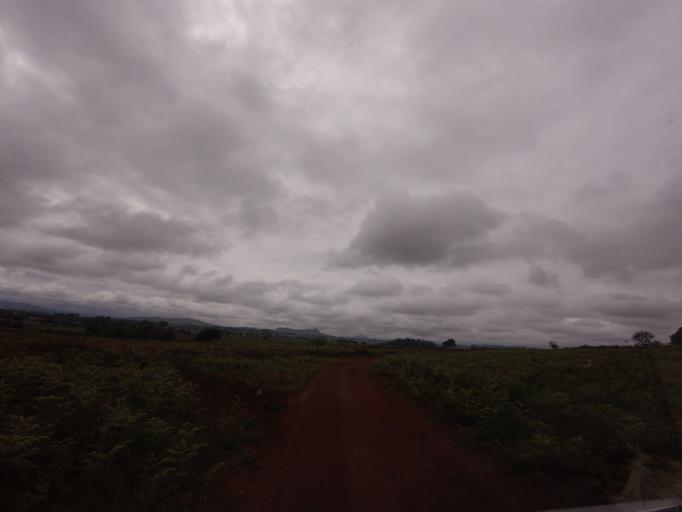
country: SZ
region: Hhohho
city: Lobamba
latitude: -26.4700
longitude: 31.1865
